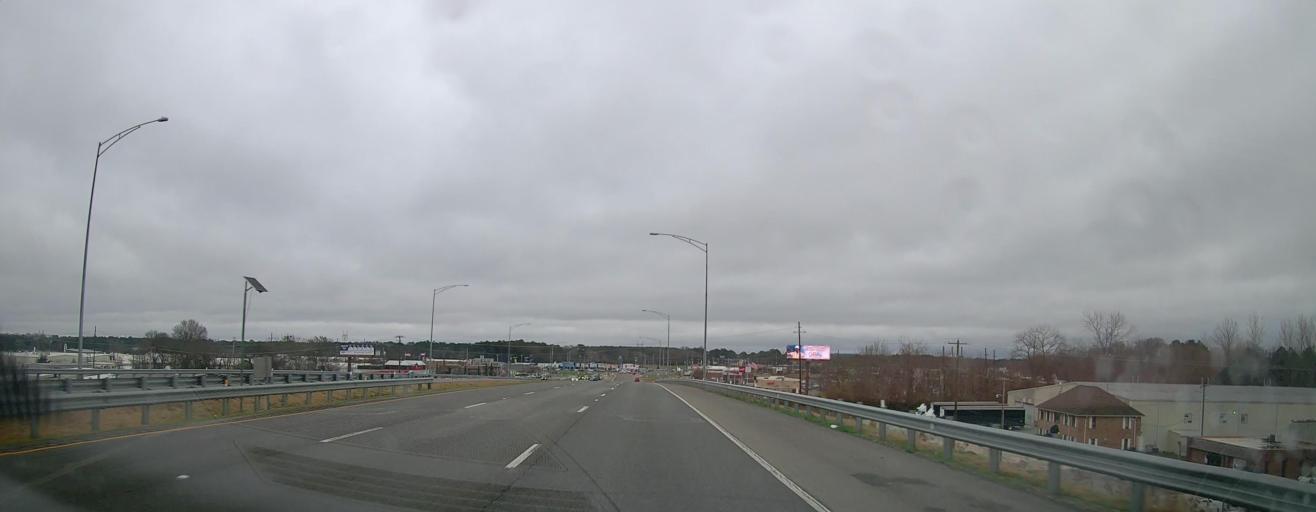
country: US
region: Alabama
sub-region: Morgan County
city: Flint City
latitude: 34.5614
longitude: -86.9805
